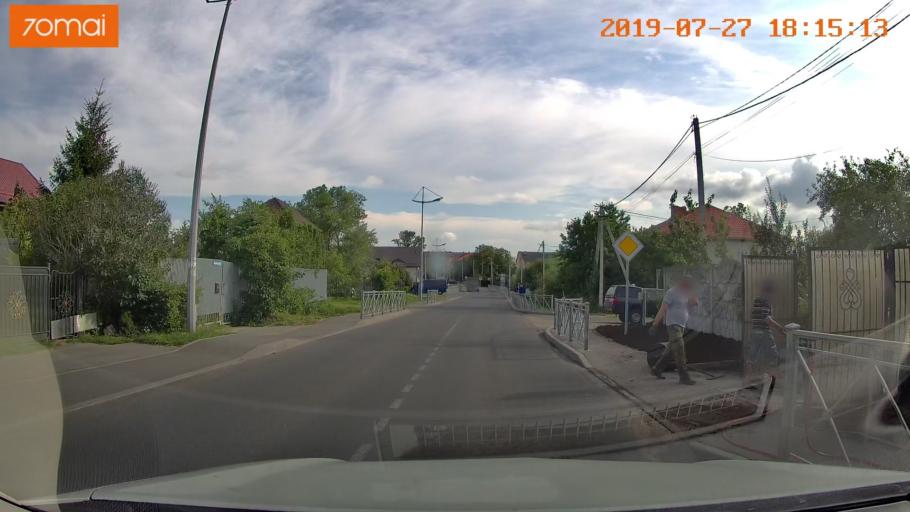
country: RU
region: Kaliningrad
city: Bol'shoe Isakovo
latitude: 54.7209
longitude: 20.6002
